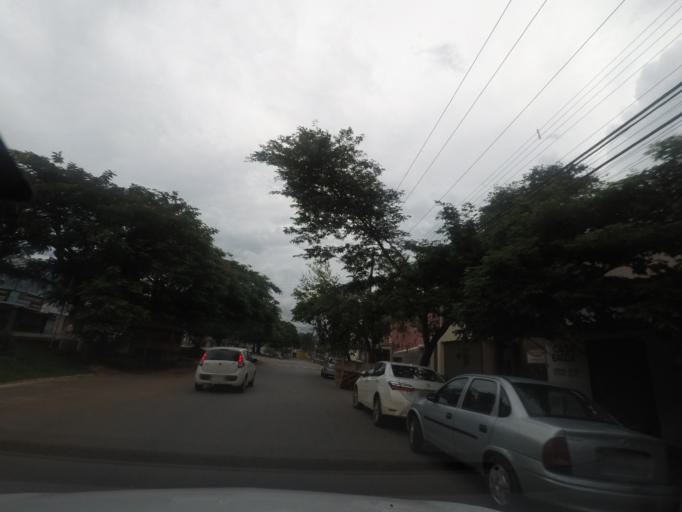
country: BR
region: Goias
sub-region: Goiania
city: Goiania
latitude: -16.7182
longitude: -49.2422
